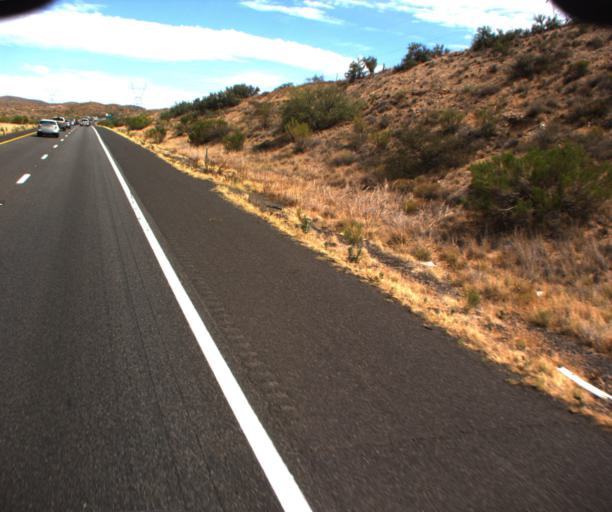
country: US
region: Arizona
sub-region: Yavapai County
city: Cordes Lakes
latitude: 34.2478
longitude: -112.1122
